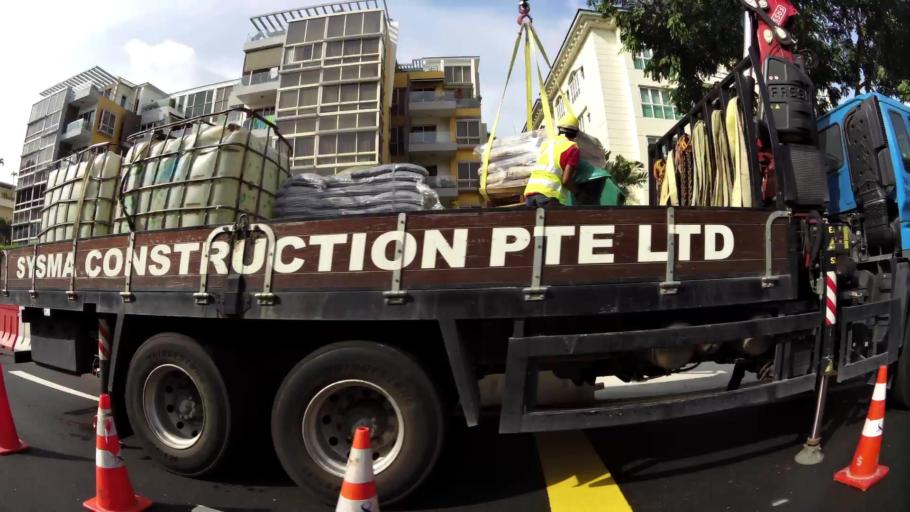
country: SG
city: Singapore
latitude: 1.2882
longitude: 103.7785
